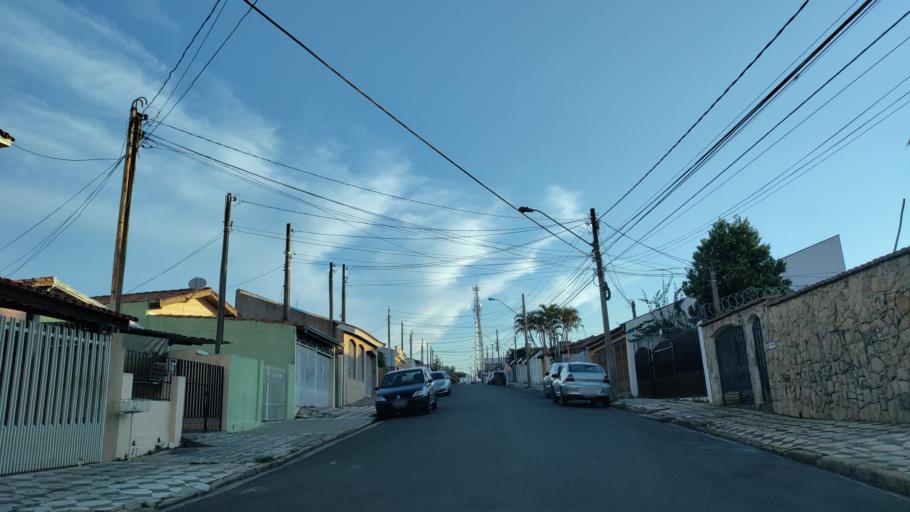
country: BR
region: Sao Paulo
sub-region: Sorocaba
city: Sorocaba
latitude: -23.4834
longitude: -47.4502
